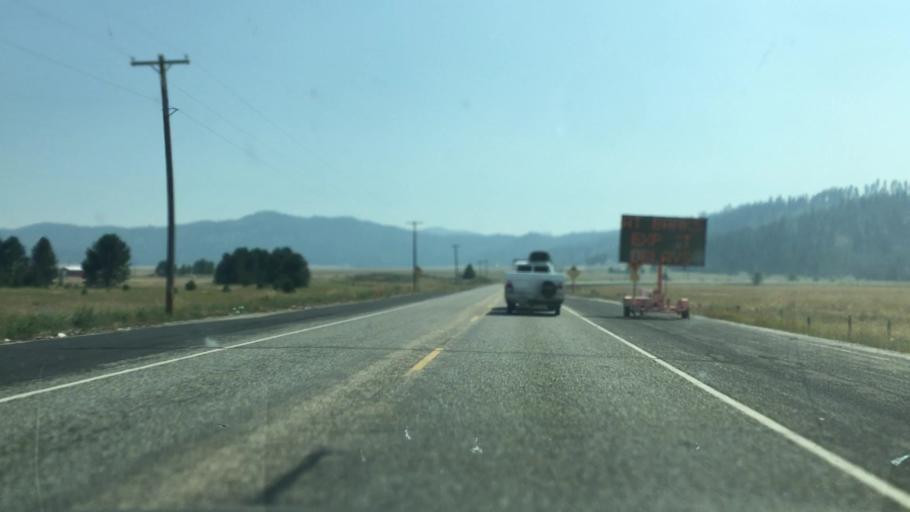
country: US
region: Idaho
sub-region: Valley County
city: Cascade
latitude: 44.3411
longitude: -116.0291
